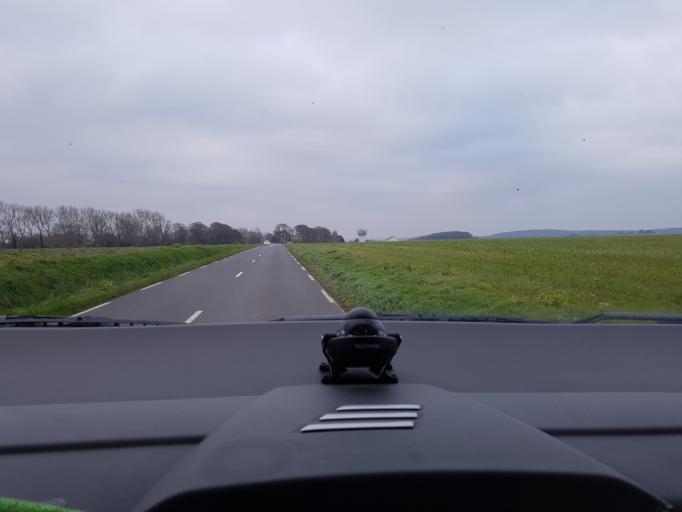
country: FR
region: Haute-Normandie
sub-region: Departement de la Seine-Maritime
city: Le Treport
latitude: 50.0333
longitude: 1.3575
